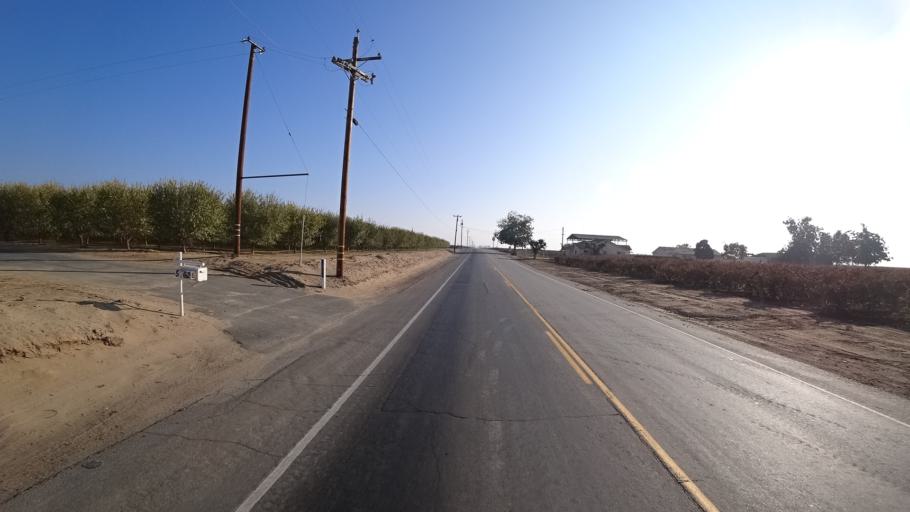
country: US
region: California
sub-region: Kern County
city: Weedpatch
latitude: 35.2378
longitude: -118.9478
